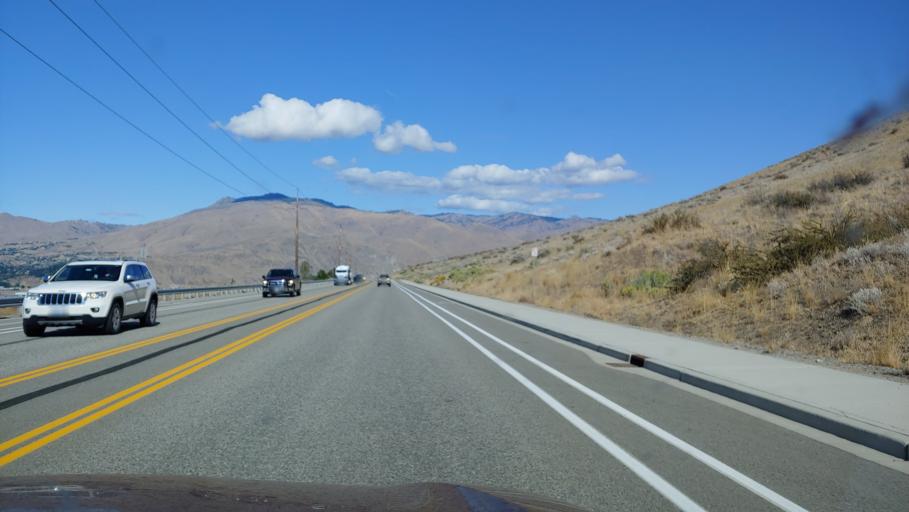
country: US
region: Washington
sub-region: Douglas County
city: East Wenatchee Bench
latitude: 47.4481
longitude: -120.2869
